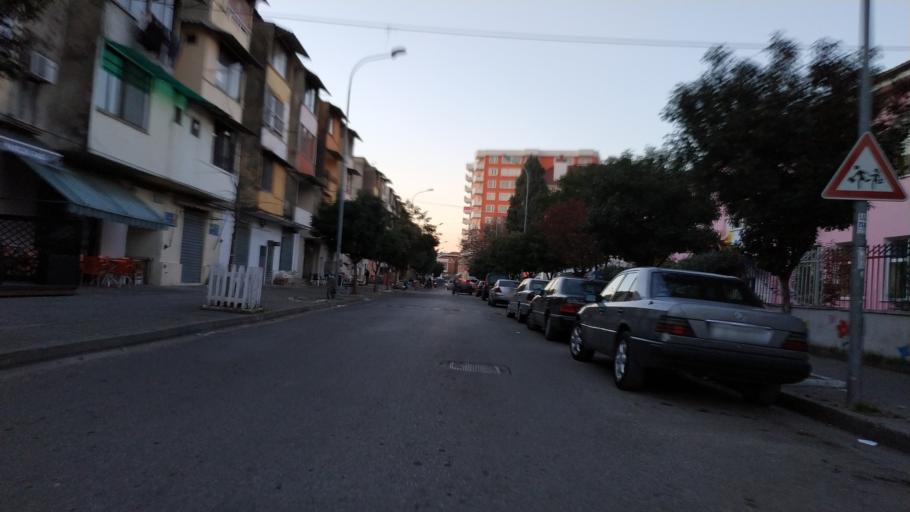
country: AL
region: Shkoder
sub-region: Rrethi i Shkodres
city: Shkoder
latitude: 42.0743
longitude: 19.5192
